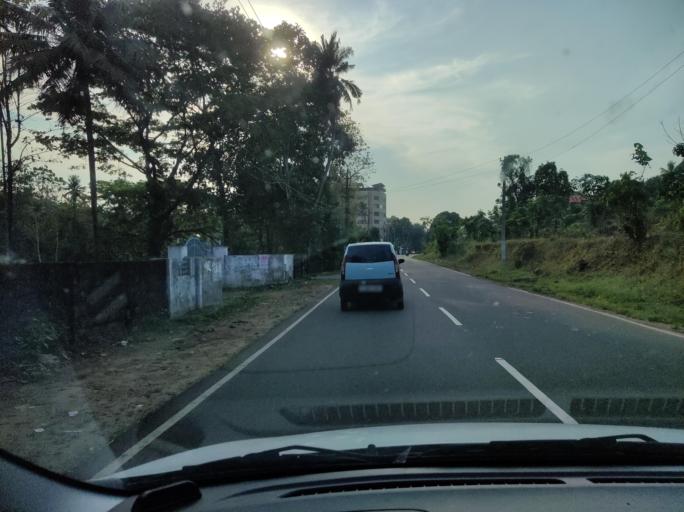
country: IN
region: Kerala
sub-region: Kottayam
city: Kottayam
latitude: 9.6440
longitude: 76.5324
